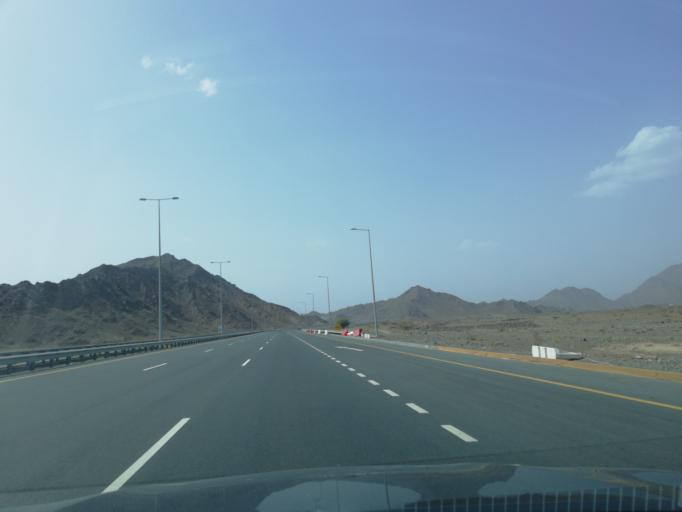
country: OM
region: Ash Sharqiyah
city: Ibra'
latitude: 22.9502
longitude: 58.2464
